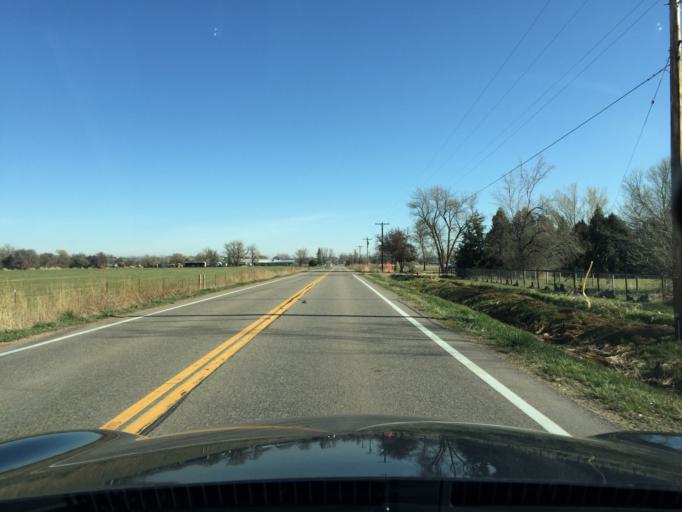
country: US
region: Colorado
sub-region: Boulder County
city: Erie
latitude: 40.0783
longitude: -105.0554
